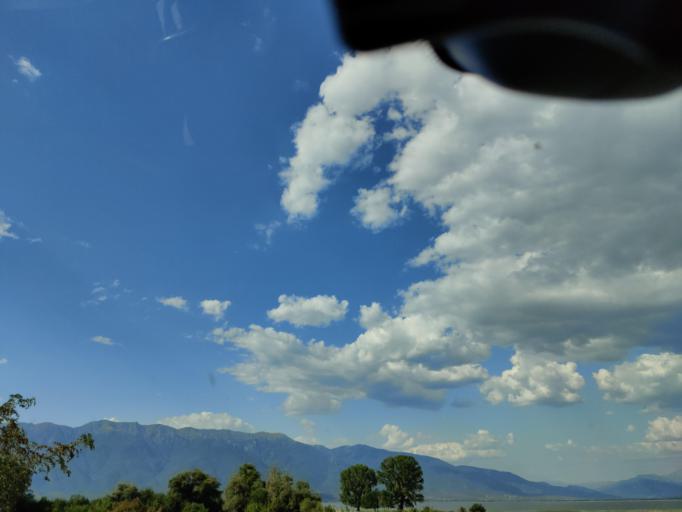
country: GR
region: Central Macedonia
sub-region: Nomos Serron
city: Chrysochorafa
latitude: 41.1852
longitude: 23.1079
